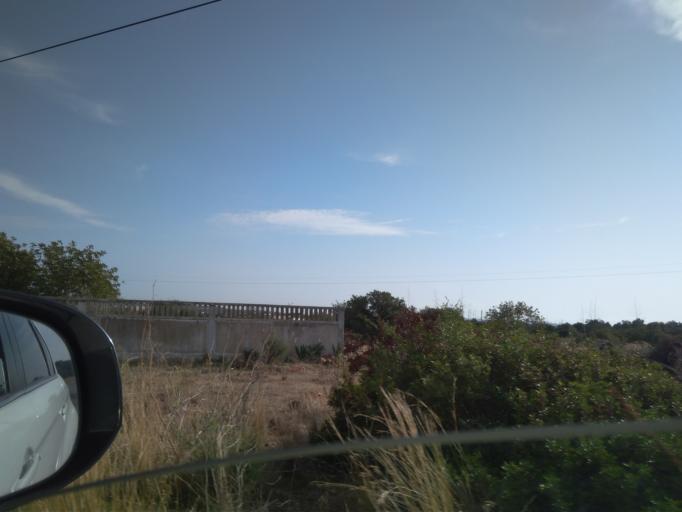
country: PT
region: Faro
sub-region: Faro
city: Santa Barbara de Nexe
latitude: 37.0907
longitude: -7.9330
